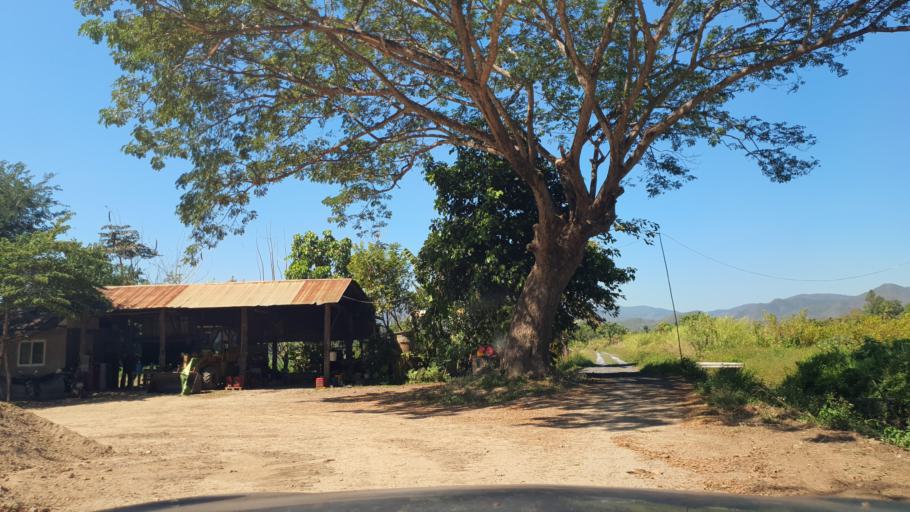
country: TH
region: Chiang Mai
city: Mae Wang
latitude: 18.6702
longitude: 98.8295
